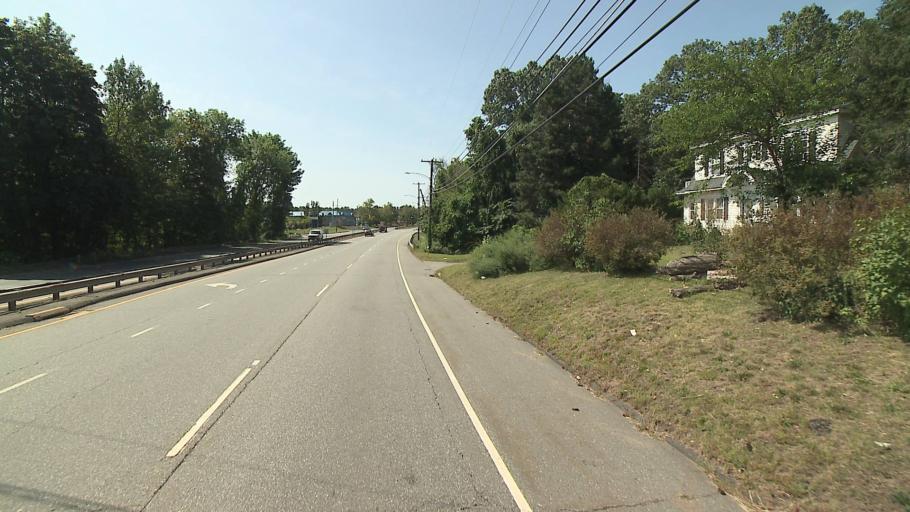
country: US
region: Connecticut
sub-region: Hartford County
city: East Hartford
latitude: 41.7978
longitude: -72.6197
